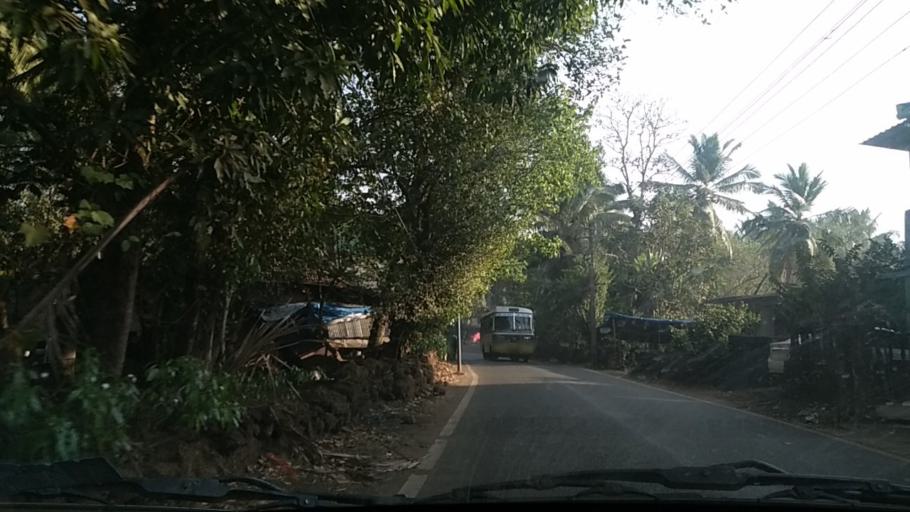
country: IN
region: Goa
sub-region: South Goa
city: Cuncolim
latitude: 15.1818
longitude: 74.0013
